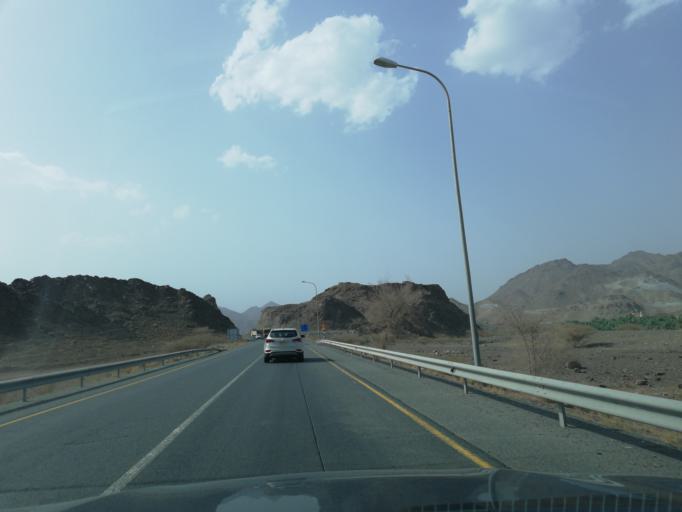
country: OM
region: Muhafazat ad Dakhiliyah
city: Sufalat Sama'il
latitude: 23.2062
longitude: 58.0811
